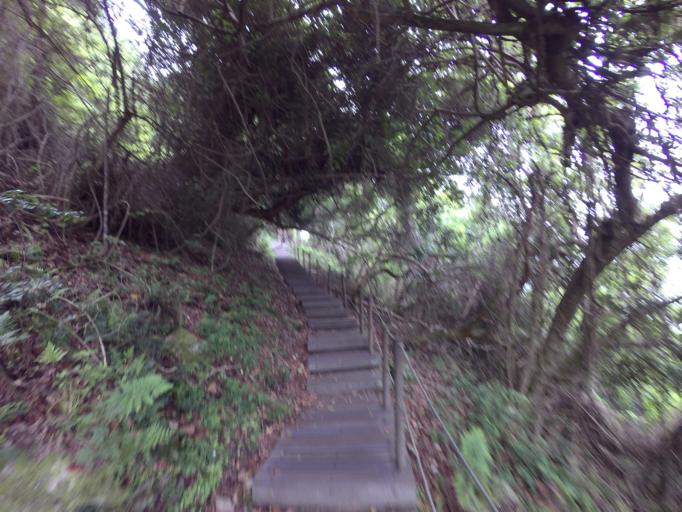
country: ZA
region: Eastern Cape
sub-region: Cacadu District Municipality
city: Kareedouw
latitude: -34.0207
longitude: 23.8996
